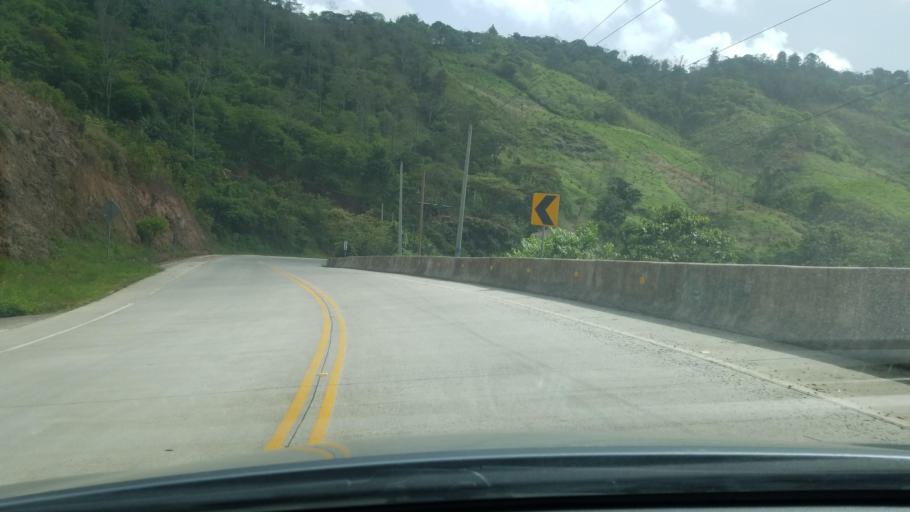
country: HN
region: Copan
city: Buenos Aires
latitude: 14.9306
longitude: -88.9646
